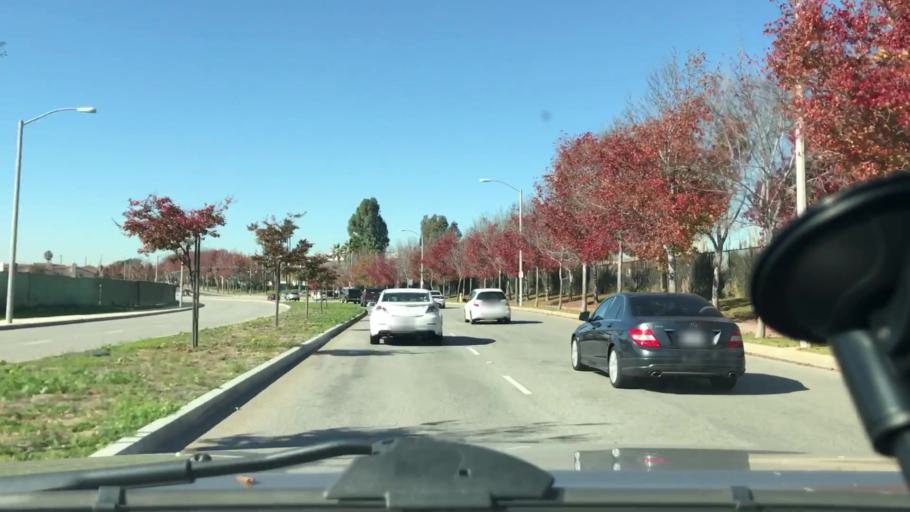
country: US
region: California
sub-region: Los Angeles County
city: Torrance
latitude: 33.8482
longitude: -118.3429
